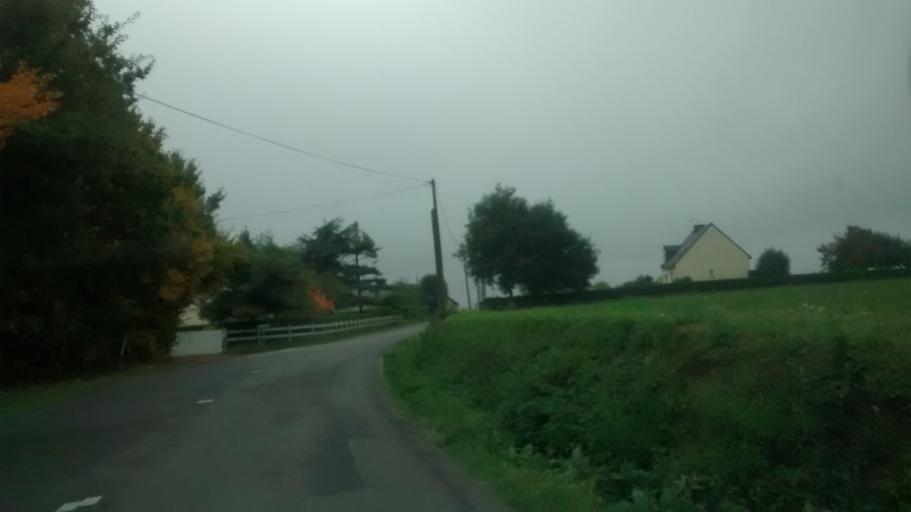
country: FR
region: Brittany
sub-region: Departement d'Ille-et-Vilaine
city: Pace
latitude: 48.1450
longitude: -1.7958
